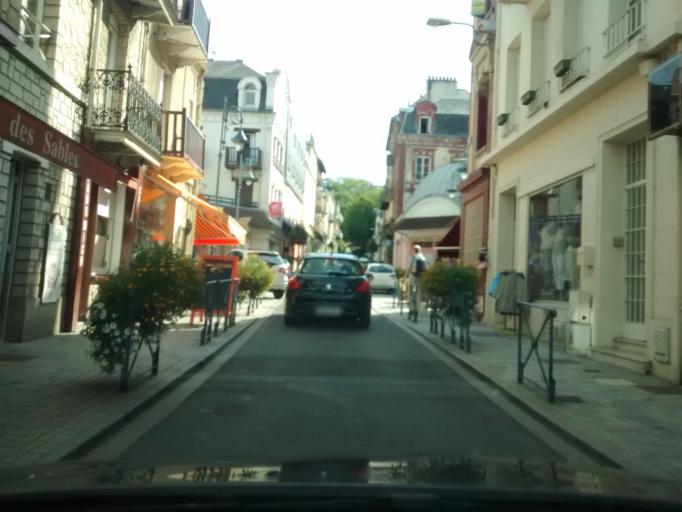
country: FR
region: Lower Normandy
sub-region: Departement du Calvados
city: Villers-sur-Mer
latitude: 49.3224
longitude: -0.0063
